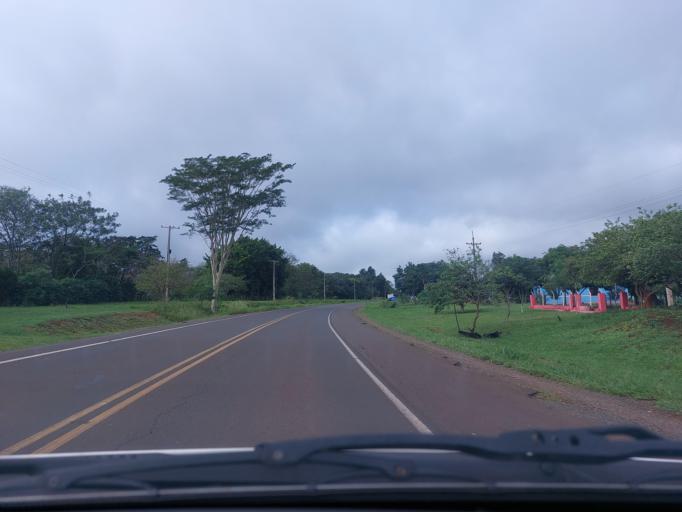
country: PY
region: San Pedro
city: Guayaybi
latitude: -24.6050
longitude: -56.3831
